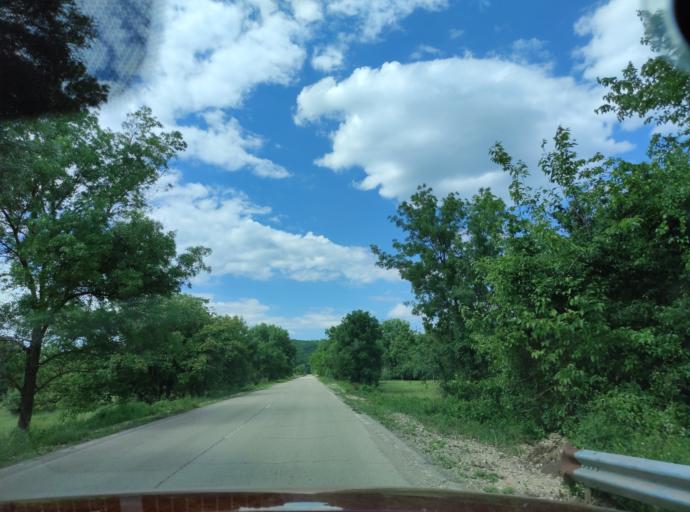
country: BG
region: Montana
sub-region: Obshtina Montana
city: Montana
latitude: 43.3975
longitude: 23.0725
